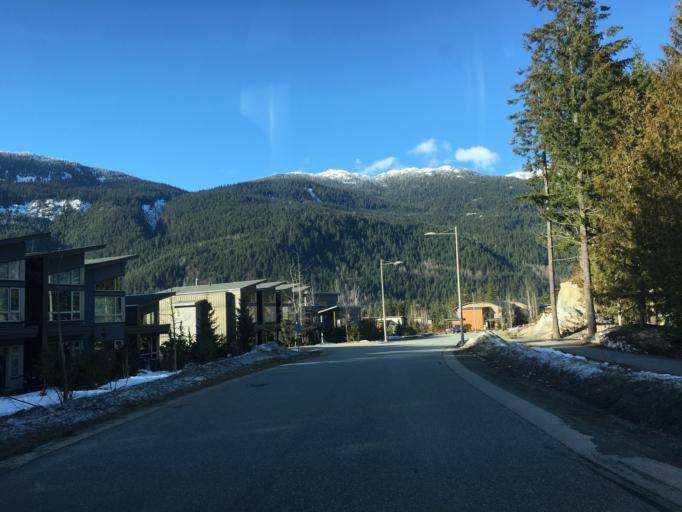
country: CA
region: British Columbia
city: Whistler
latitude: 50.0774
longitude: -123.0389
